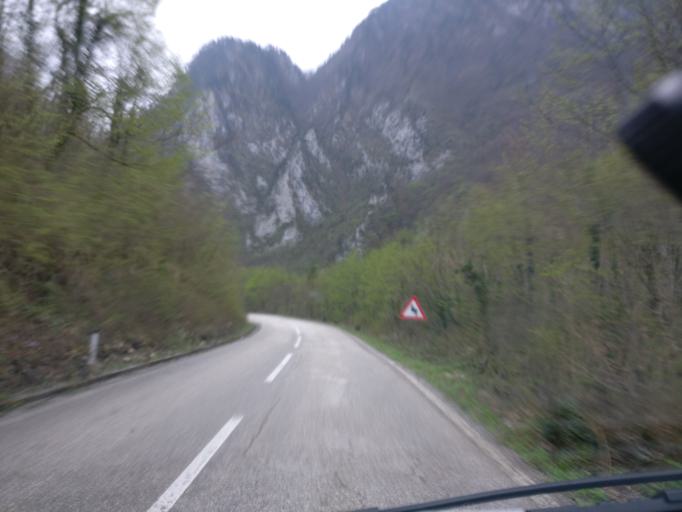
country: ME
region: Opstina Pluzine
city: Pluzine
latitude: 43.3058
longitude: 18.8507
